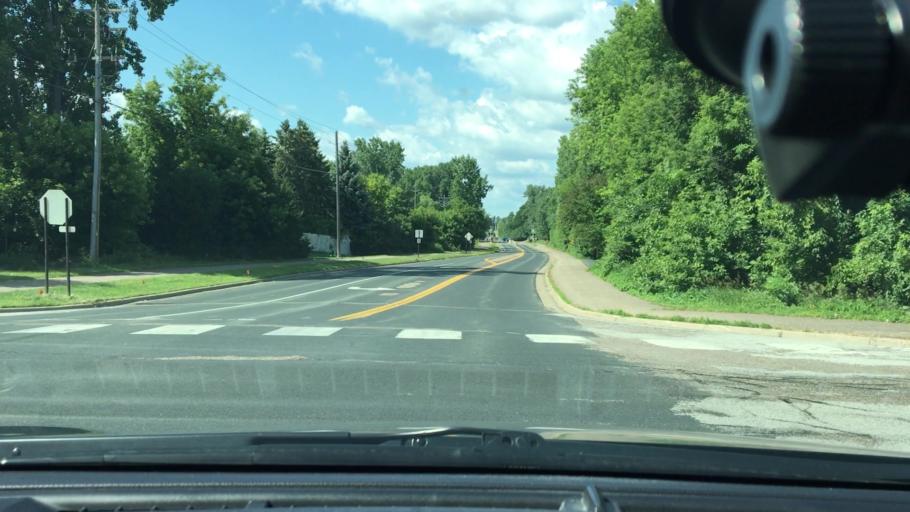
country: US
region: Minnesota
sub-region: Hennepin County
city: New Hope
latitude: 45.0474
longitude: -93.4209
